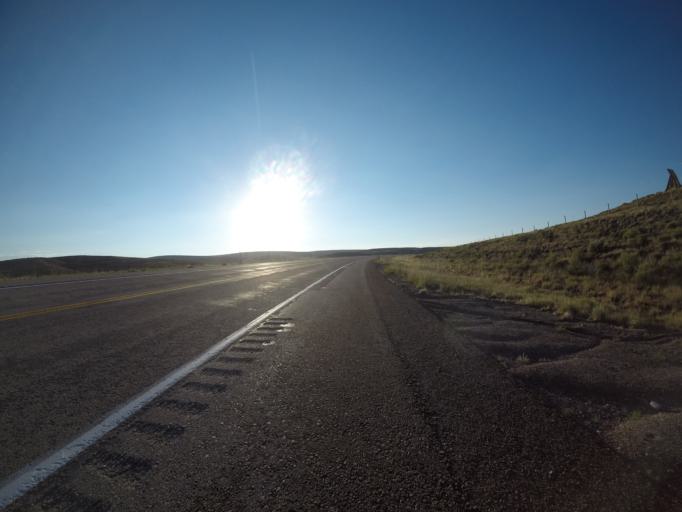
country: US
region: Wyoming
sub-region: Lincoln County
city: Kemmerer
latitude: 41.8748
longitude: -110.4849
